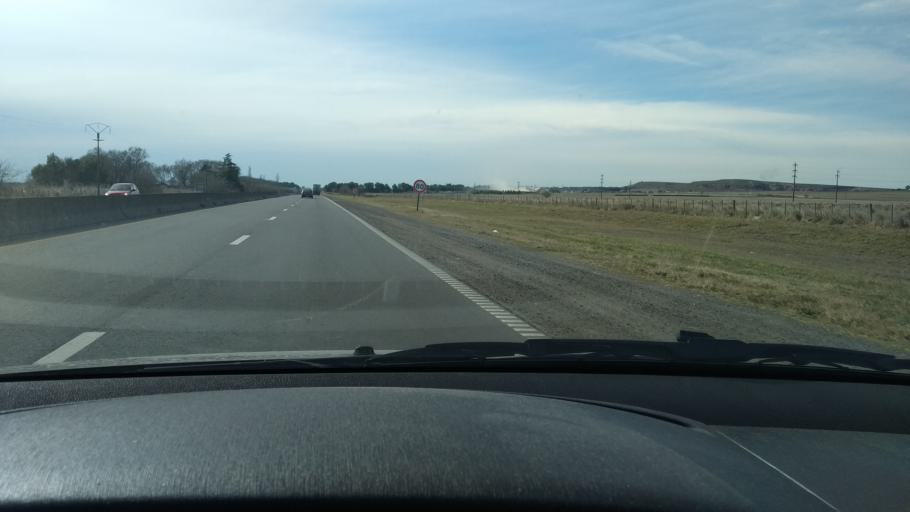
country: AR
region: Buenos Aires
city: Olavarria
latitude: -36.9308
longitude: -60.2225
